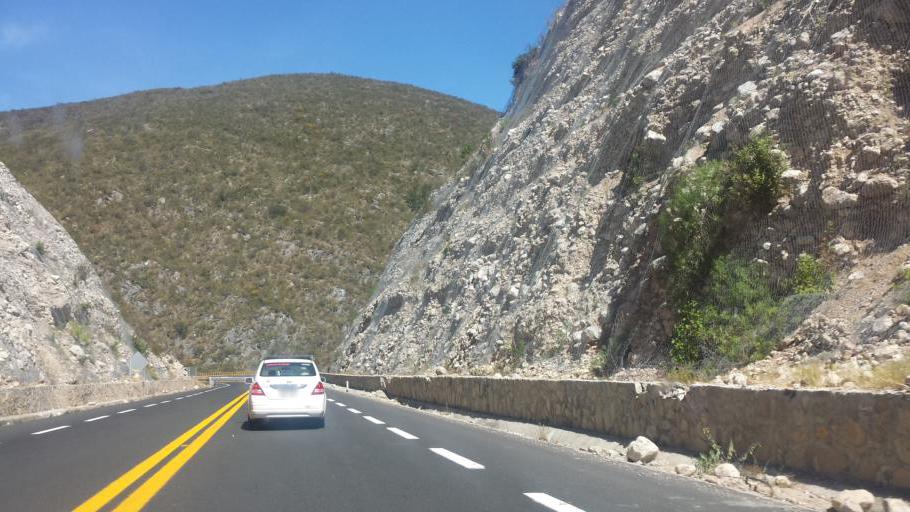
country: MX
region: Puebla
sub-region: San Jose Miahuatlan
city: San Pedro Tetitlan
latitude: 18.0240
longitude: -97.3483
